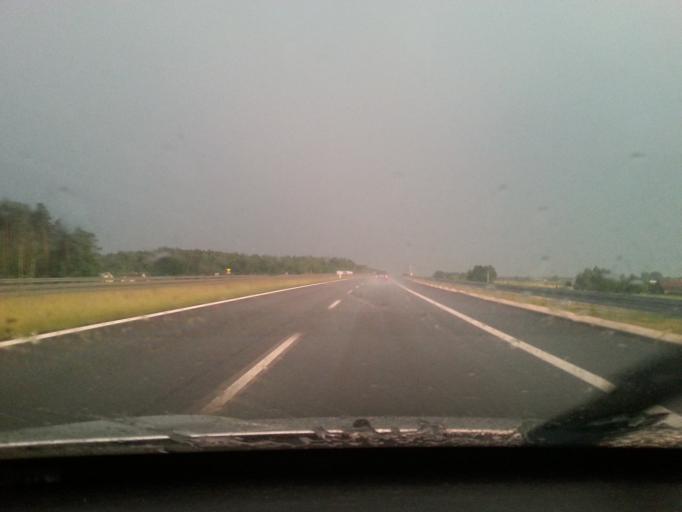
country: PL
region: Lodz Voivodeship
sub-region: Powiat pabianicki
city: Dobron
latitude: 51.6183
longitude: 19.2749
